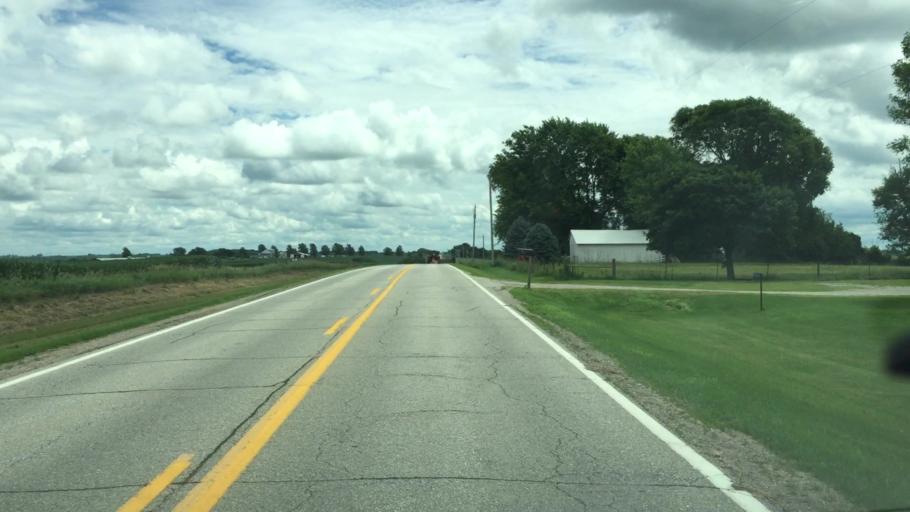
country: US
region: Iowa
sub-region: Jasper County
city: Monroe
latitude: 41.5735
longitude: -93.0881
